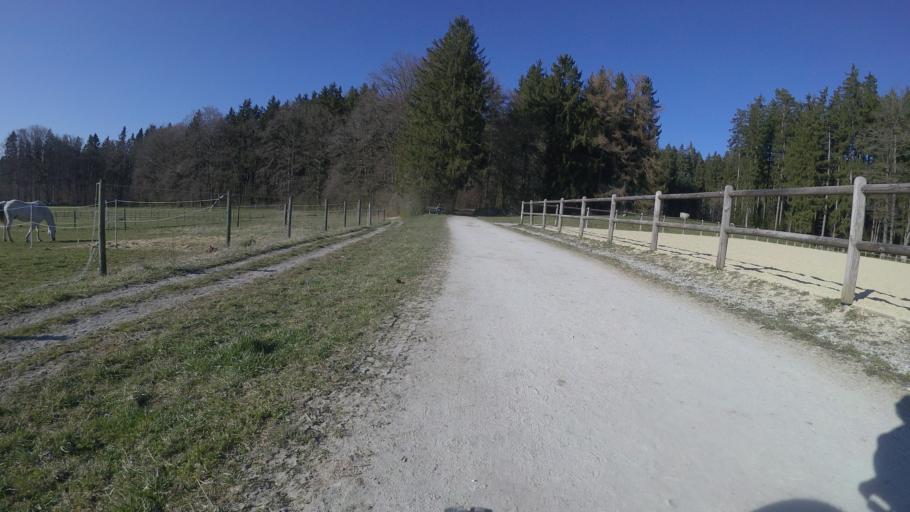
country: DE
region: Bavaria
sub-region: Upper Bavaria
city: Chieming
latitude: 47.9321
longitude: 12.5433
